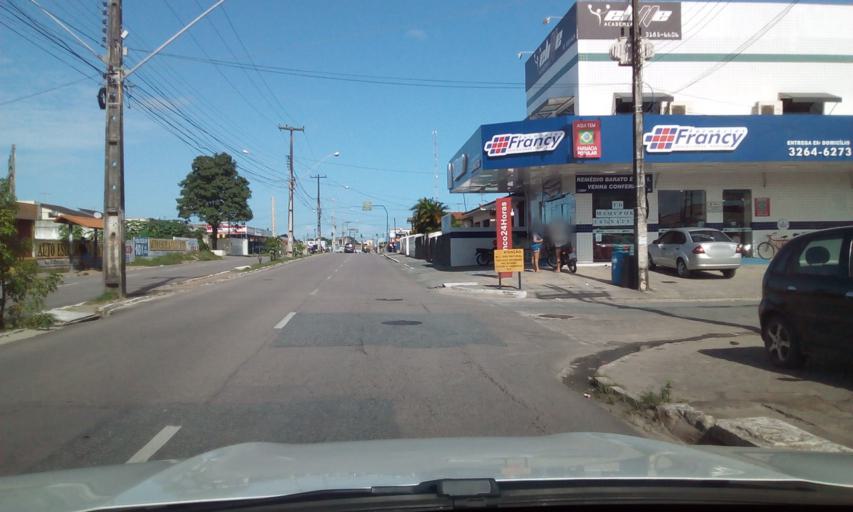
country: BR
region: Paraiba
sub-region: Joao Pessoa
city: Joao Pessoa
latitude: -7.1609
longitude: -34.8707
